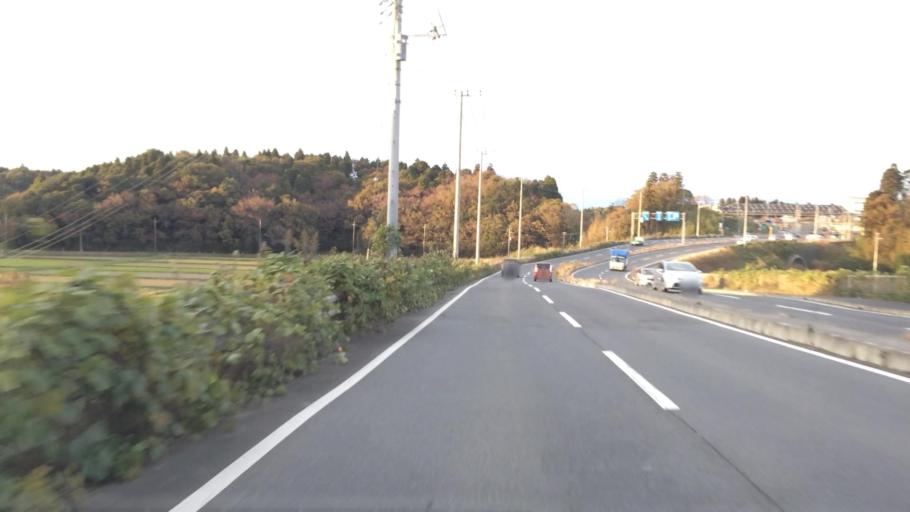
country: JP
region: Chiba
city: Shisui
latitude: 35.7202
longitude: 140.2944
